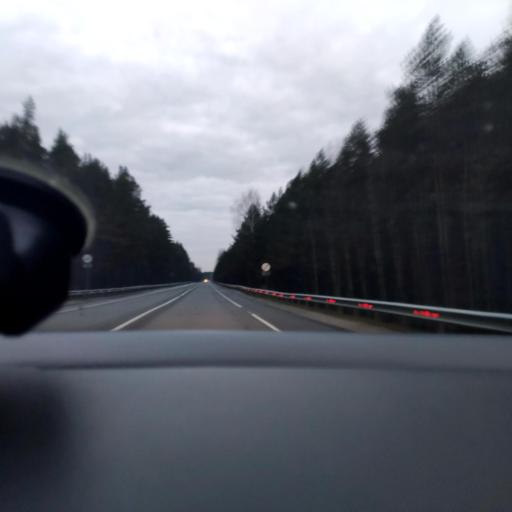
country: RU
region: Moskovskaya
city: Il'inskiy Pogost
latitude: 55.4798
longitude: 38.9383
